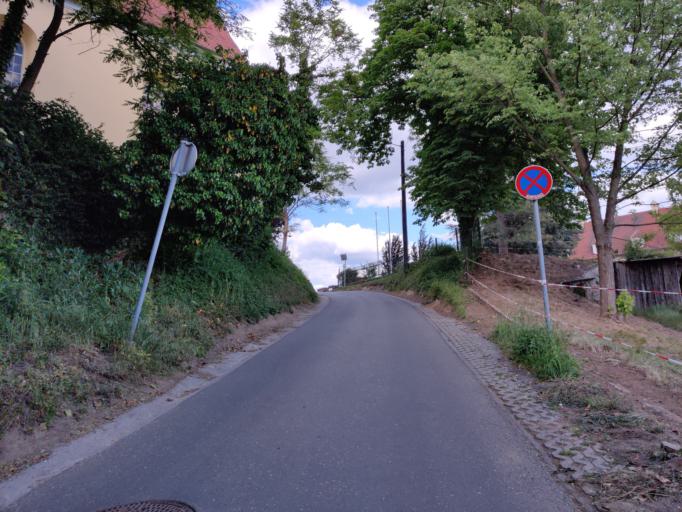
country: AT
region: Styria
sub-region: Graz Stadt
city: Wetzelsdorf
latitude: 47.0356
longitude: 15.3885
